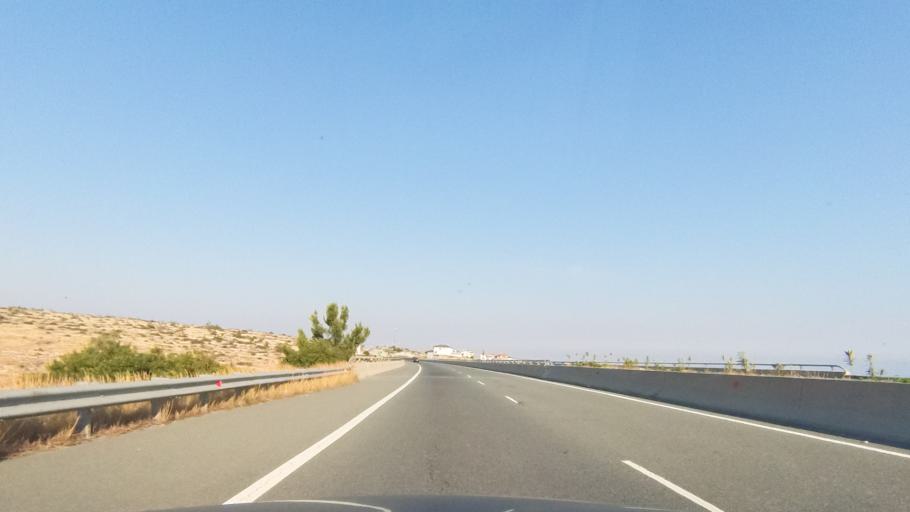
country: CY
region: Limassol
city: Sotira
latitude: 34.6839
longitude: 32.8796
